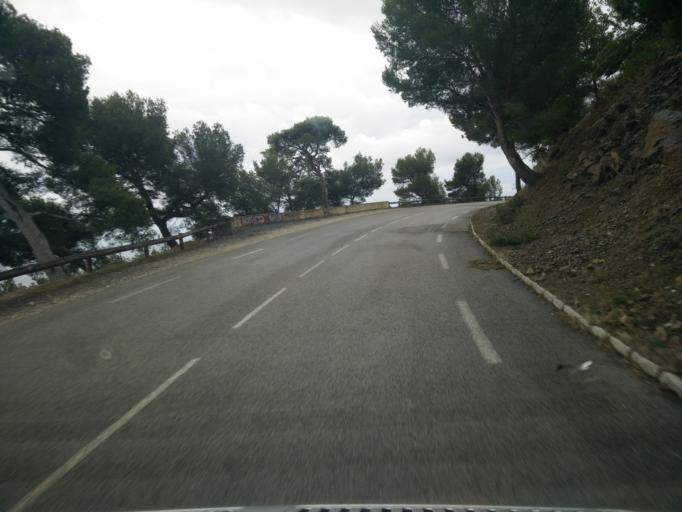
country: FR
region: Provence-Alpes-Cote d'Azur
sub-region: Departement du Var
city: Six-Fours-les-Plages
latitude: 43.0622
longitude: 5.8649
